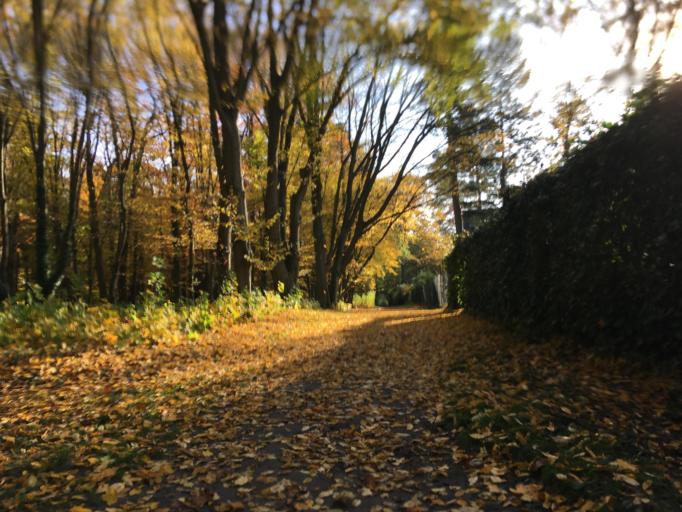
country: DE
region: Berlin
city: Frohnau
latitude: 52.6413
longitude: 13.2879
